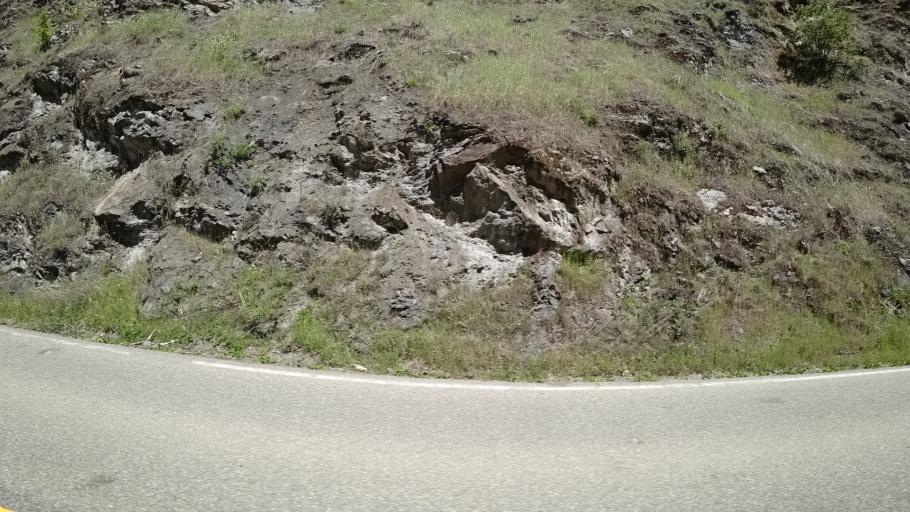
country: US
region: California
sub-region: Trinity County
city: Hayfork
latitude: 40.7713
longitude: -123.3082
